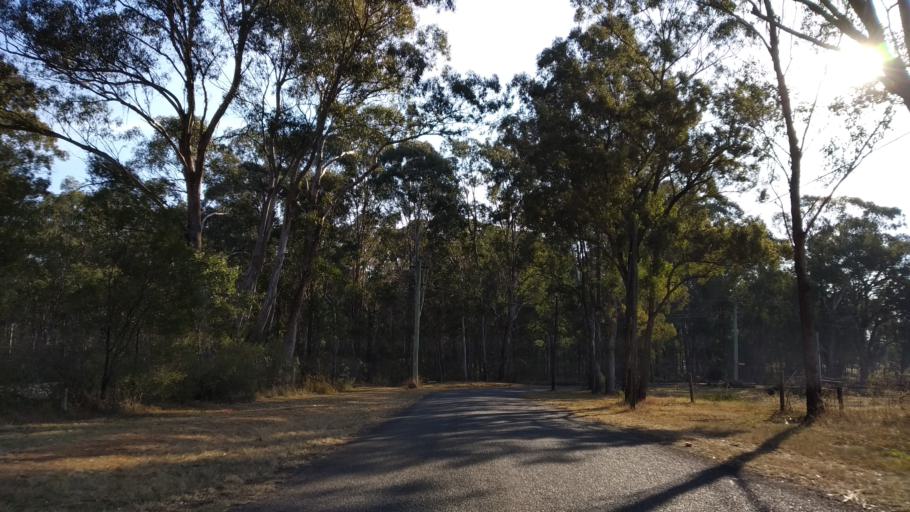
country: AU
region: New South Wales
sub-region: Penrith Municipality
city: Werrington County
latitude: -33.7172
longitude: 150.7560
